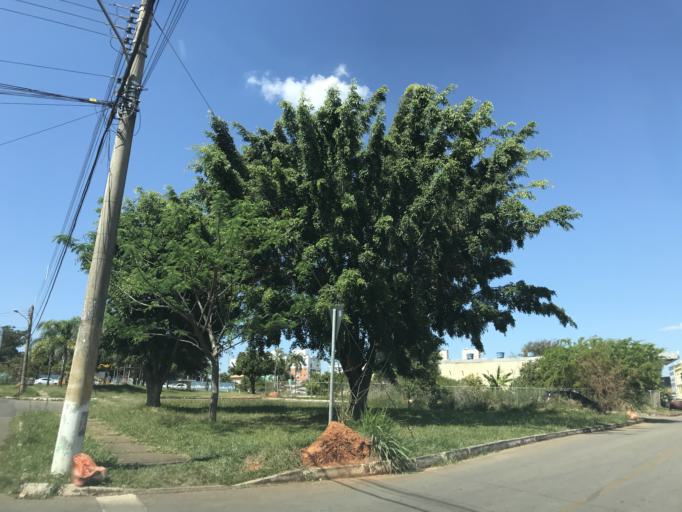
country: BR
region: Federal District
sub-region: Brasilia
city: Brasilia
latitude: -15.6601
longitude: -47.8071
